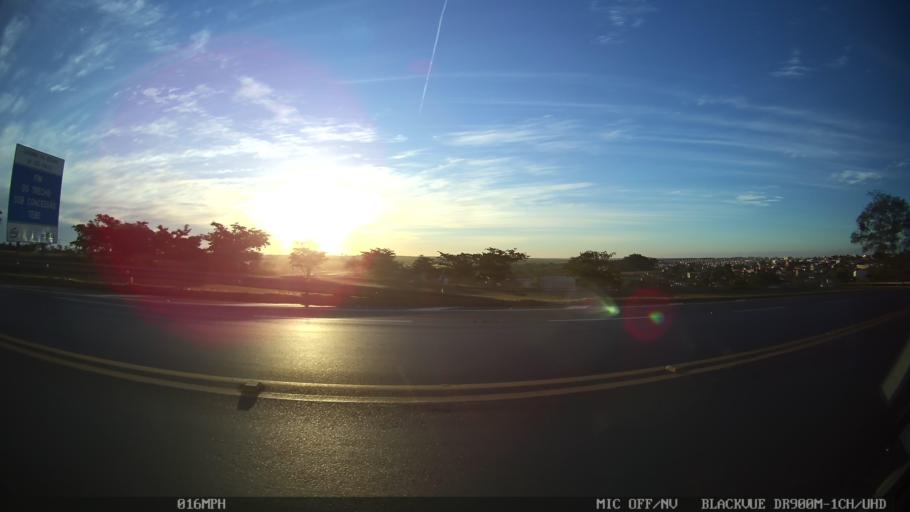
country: BR
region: Sao Paulo
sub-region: Catanduva
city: Catanduva
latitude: -21.1334
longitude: -49.0197
